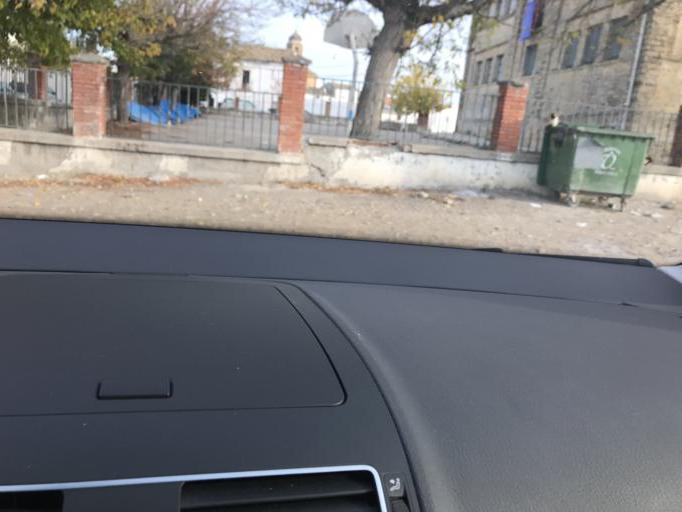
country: ES
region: Andalusia
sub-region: Provincia de Jaen
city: Ubeda
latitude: 38.0056
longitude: -3.3674
